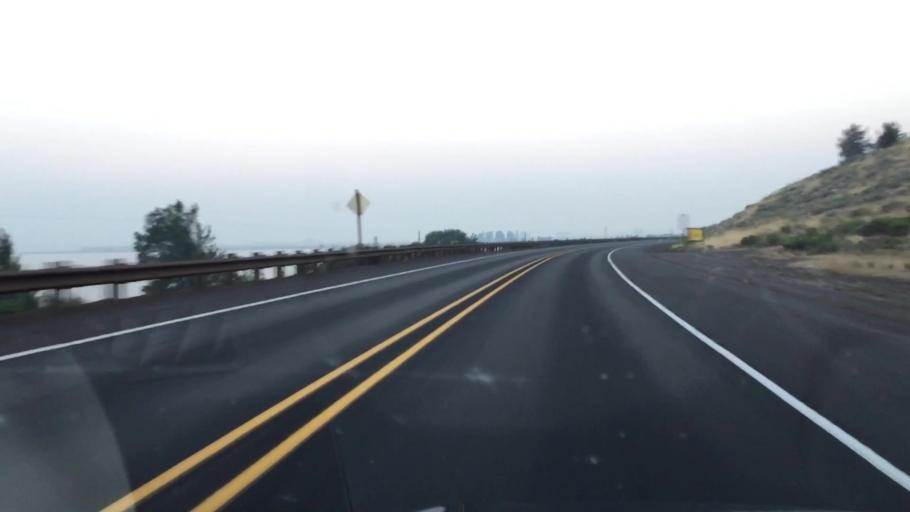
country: US
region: Oregon
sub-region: Klamath County
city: Klamath Falls
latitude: 42.4368
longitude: -121.8660
